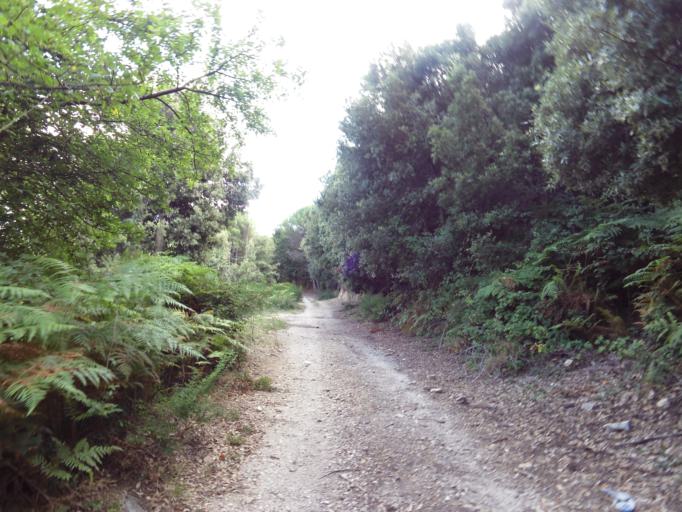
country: IT
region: Calabria
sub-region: Provincia di Reggio Calabria
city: Pazzano
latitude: 38.4762
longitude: 16.4060
